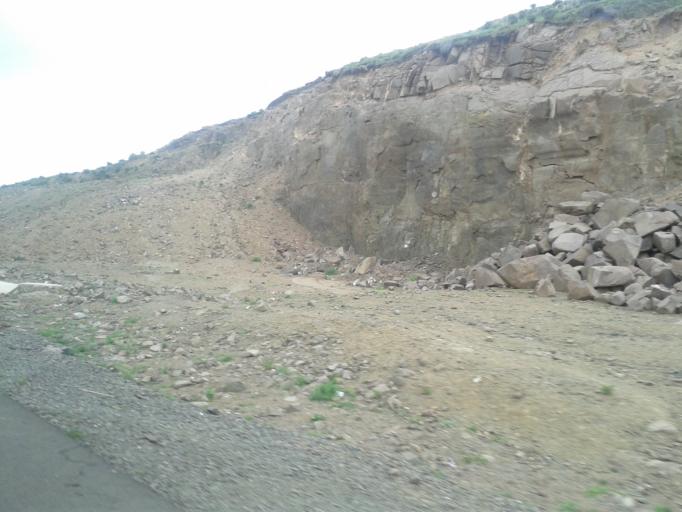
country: LS
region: Maseru
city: Nako
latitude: -29.7699
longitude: 28.0139
